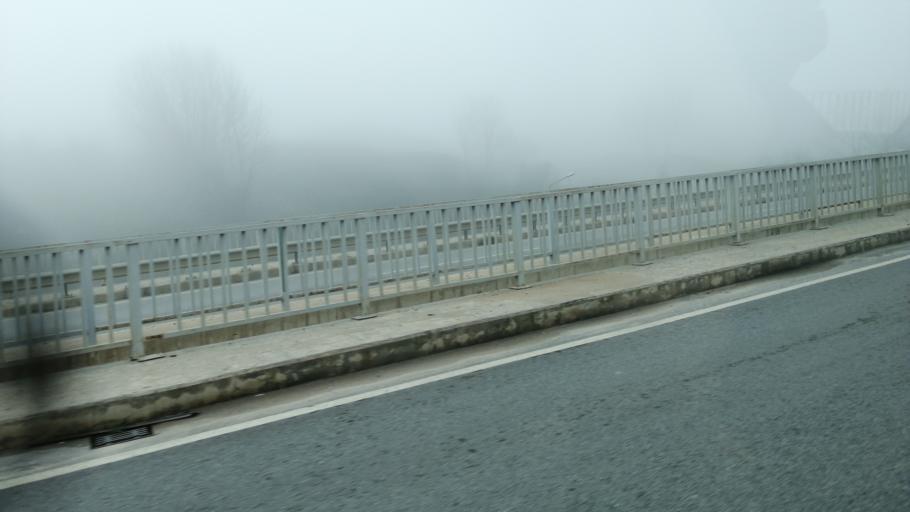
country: TR
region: Yalova
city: Kadikoy
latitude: 40.6512
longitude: 29.2184
